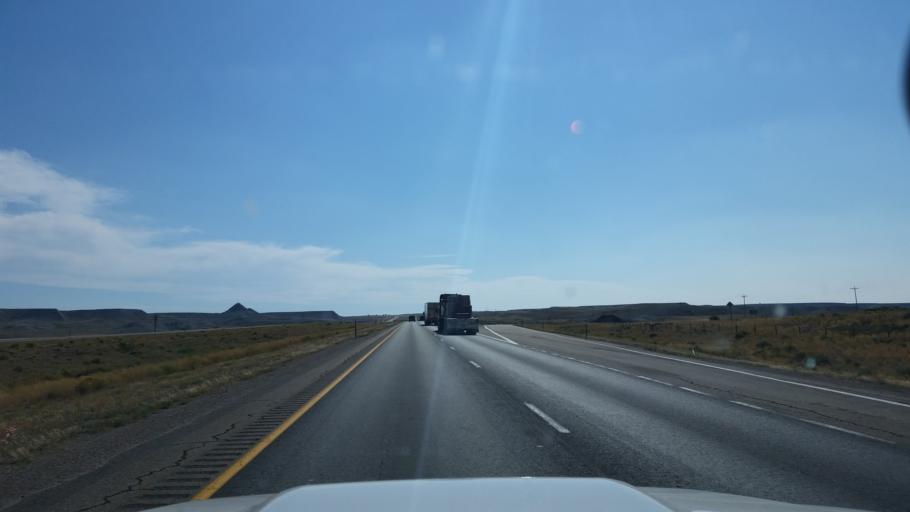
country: US
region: Wyoming
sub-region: Uinta County
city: Lyman
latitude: 41.5119
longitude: -109.9814
